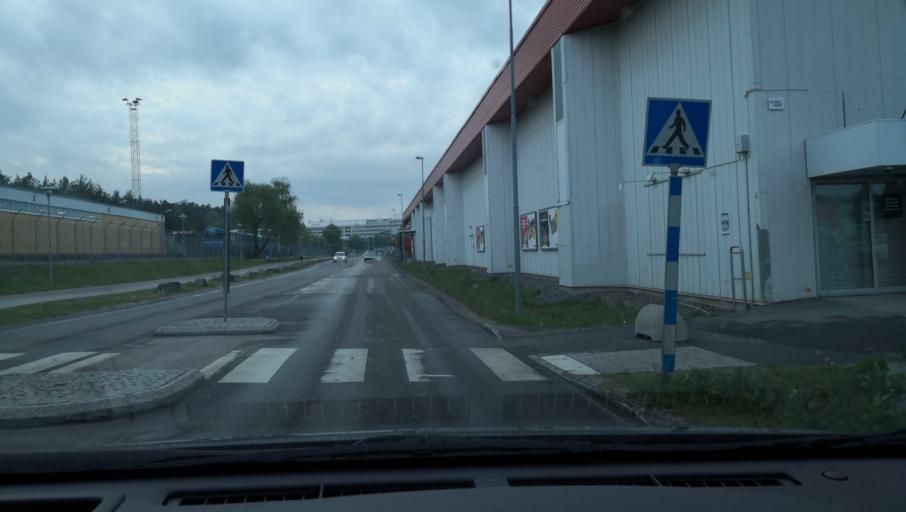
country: SE
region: Stockholm
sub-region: Stockholms Kommun
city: Kista
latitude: 59.3793
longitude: 17.9480
